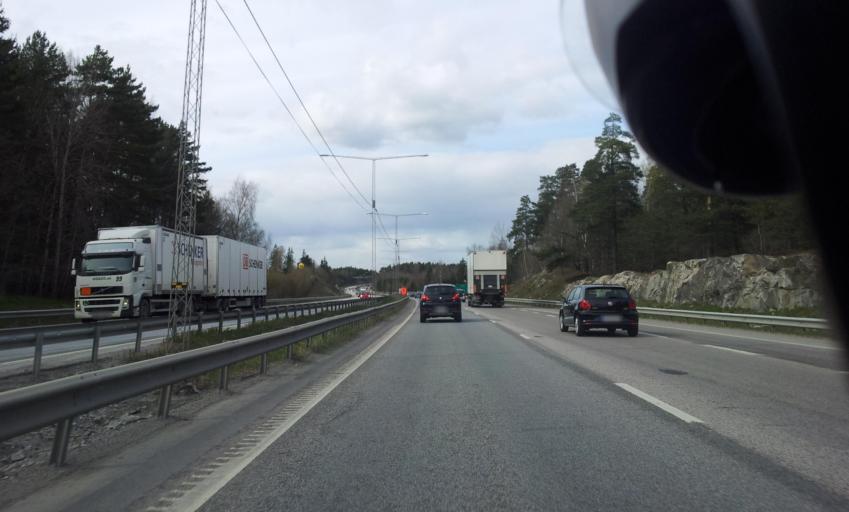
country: SE
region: Stockholm
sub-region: Jarfalla Kommun
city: Jakobsberg
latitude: 59.4265
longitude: 17.8505
